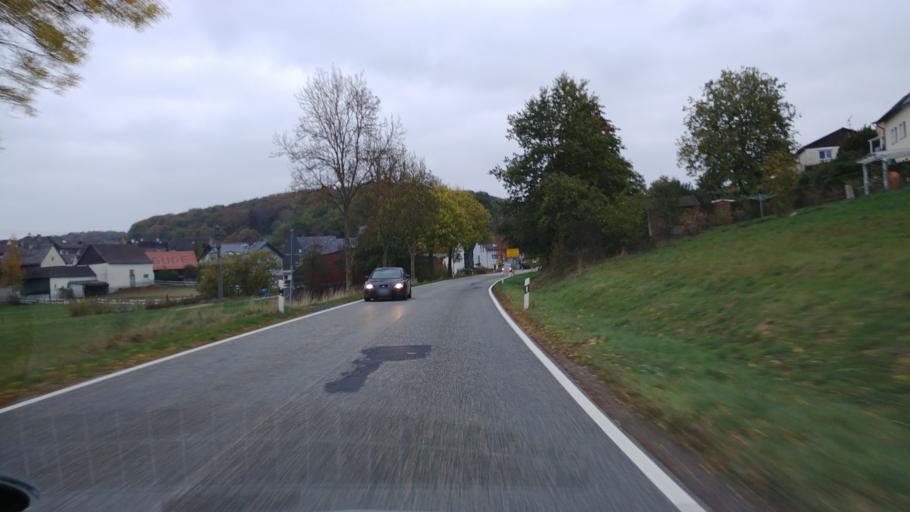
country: DE
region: Rheinland-Pfalz
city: Kaltenholzhausen
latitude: 50.2635
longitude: 8.1498
